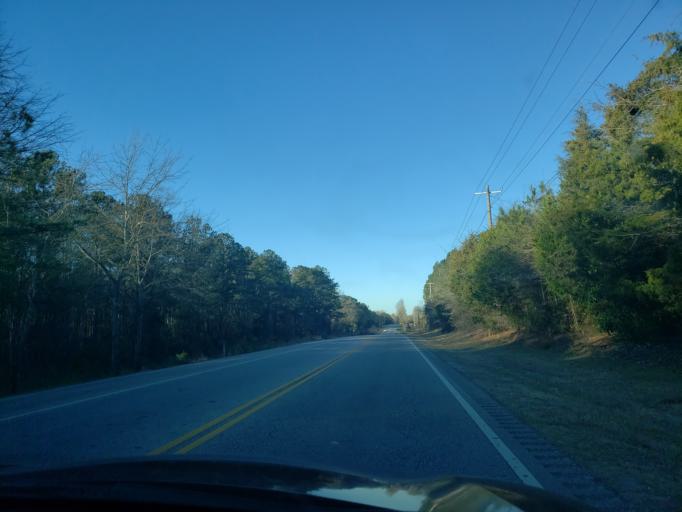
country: US
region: Alabama
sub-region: Lee County
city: Auburn
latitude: 32.6074
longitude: -85.5091
